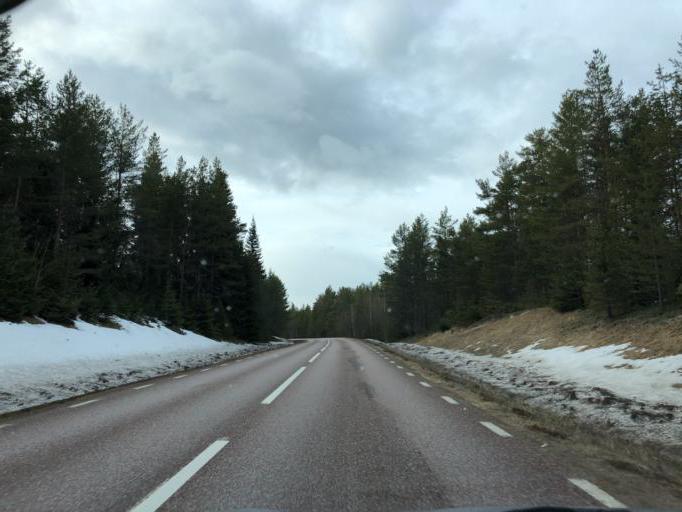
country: NO
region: Hedmark
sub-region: Trysil
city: Innbygda
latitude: 61.7444
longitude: 12.9741
